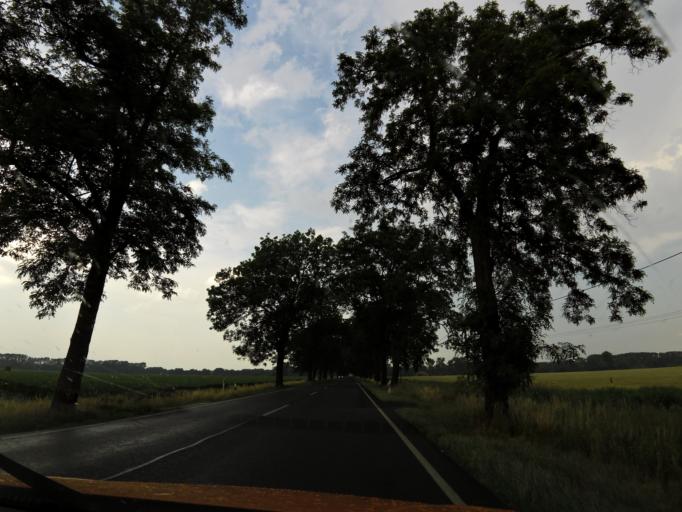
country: DE
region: Brandenburg
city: Friesack
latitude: 52.7659
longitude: 12.5654
